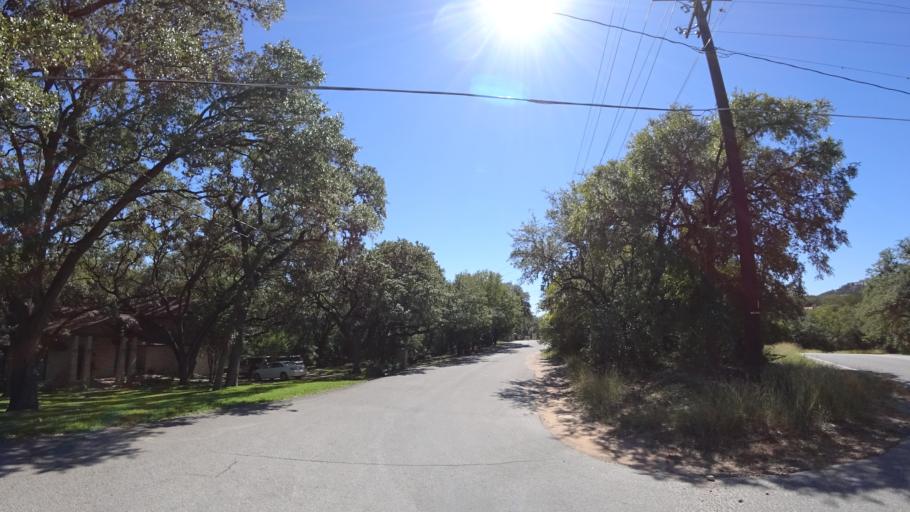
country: US
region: Texas
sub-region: Travis County
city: West Lake Hills
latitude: 30.3131
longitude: -97.7805
